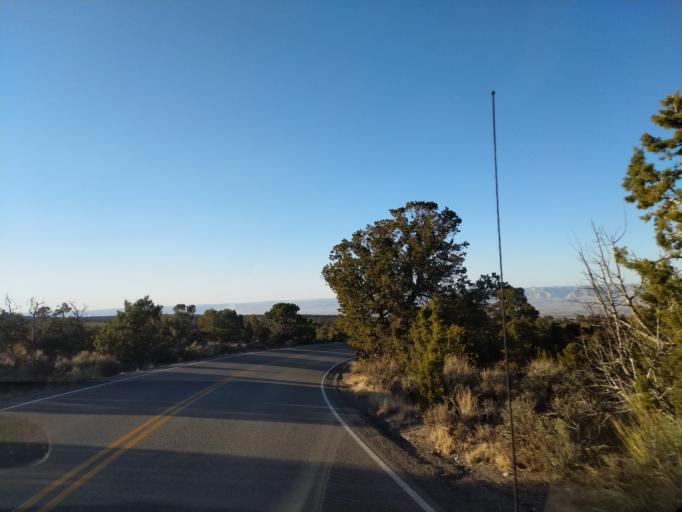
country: US
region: Colorado
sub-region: Mesa County
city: Redlands
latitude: 39.0229
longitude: -108.6601
